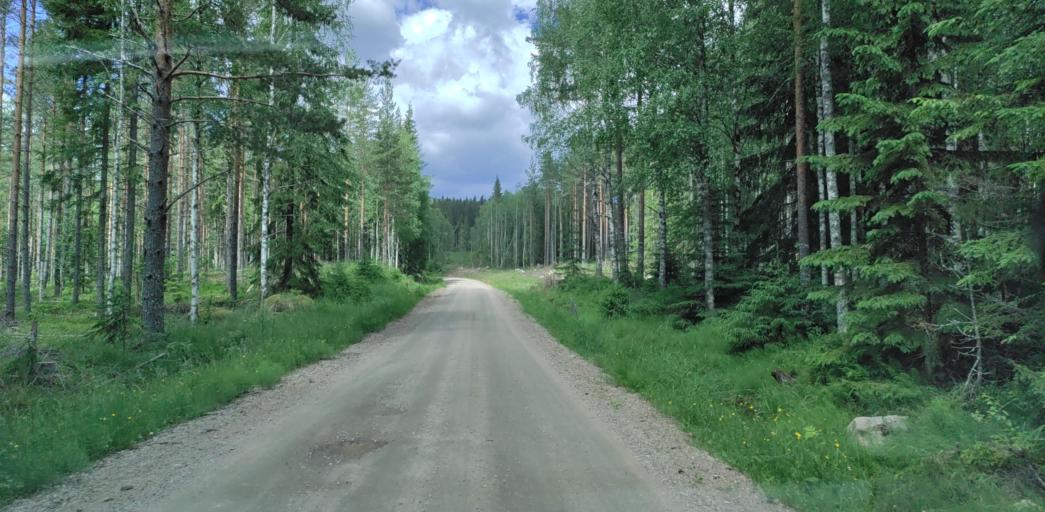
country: SE
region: Vaermland
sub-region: Hagfors Kommun
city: Ekshaerad
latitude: 60.0953
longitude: 13.4026
